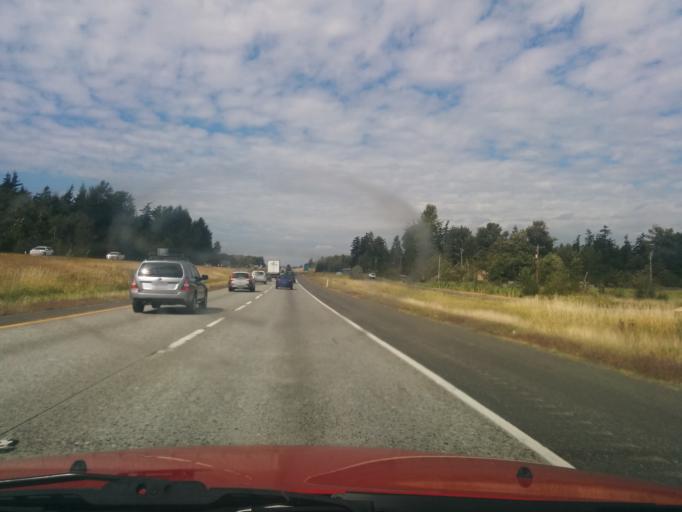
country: US
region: Washington
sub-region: Whatcom County
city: Marietta-Alderwood
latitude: 48.7989
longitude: -122.5302
